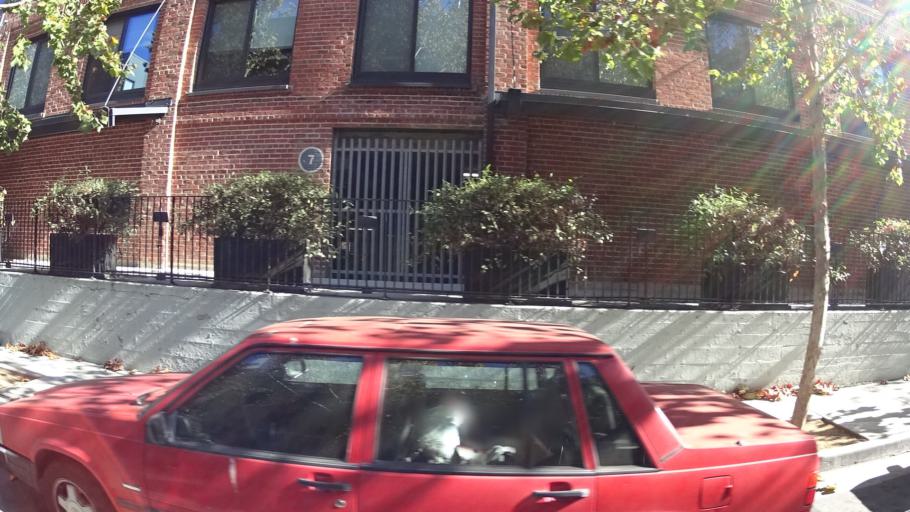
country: US
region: California
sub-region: Santa Clara County
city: San Jose
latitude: 37.3306
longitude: -121.9046
